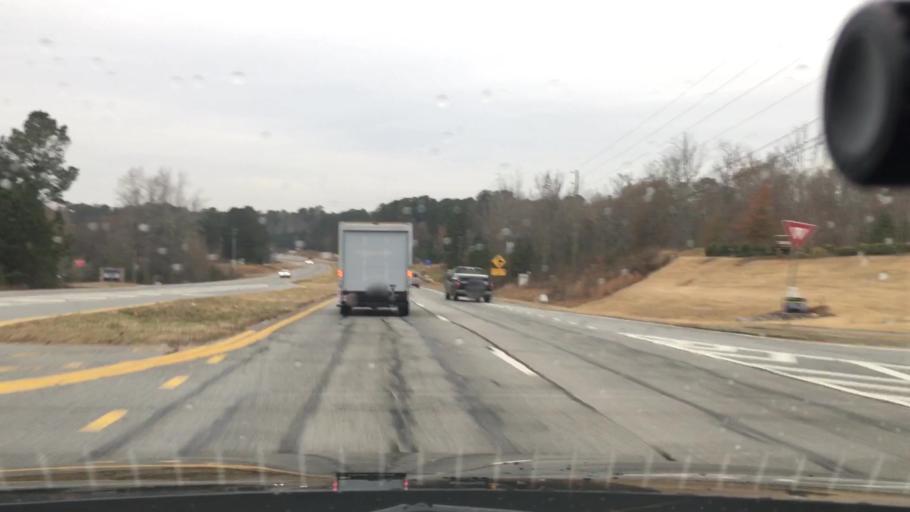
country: US
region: Georgia
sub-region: Fayette County
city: Peachtree City
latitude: 33.3997
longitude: -84.6267
